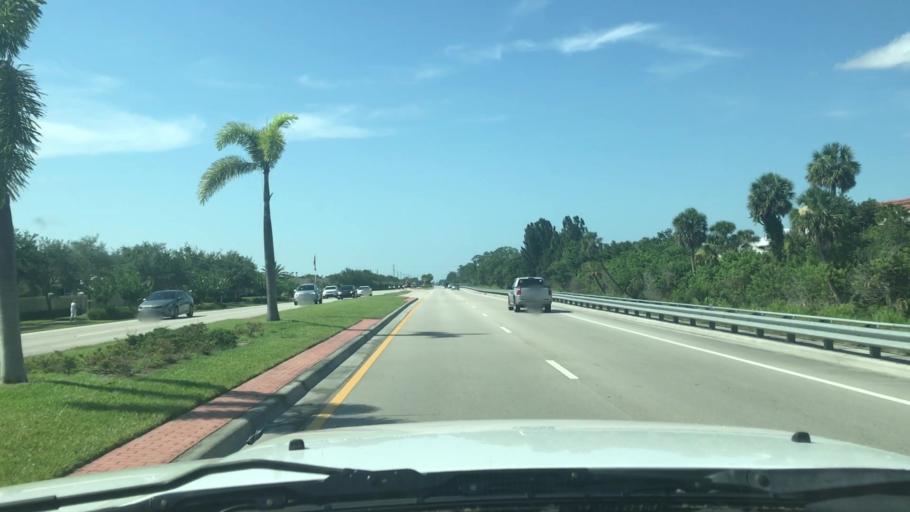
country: US
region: Florida
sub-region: Indian River County
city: West Vero Corridor
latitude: 27.6478
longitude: -80.4632
